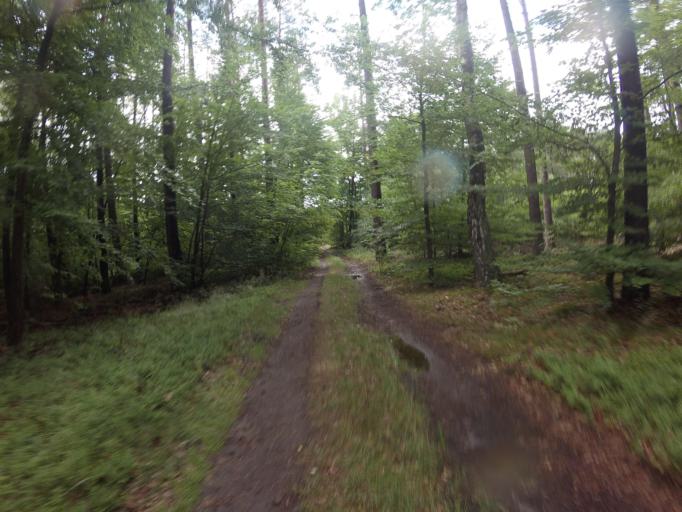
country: PL
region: West Pomeranian Voivodeship
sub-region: Powiat choszczenski
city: Bierzwnik
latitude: 53.0134
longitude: 15.5915
